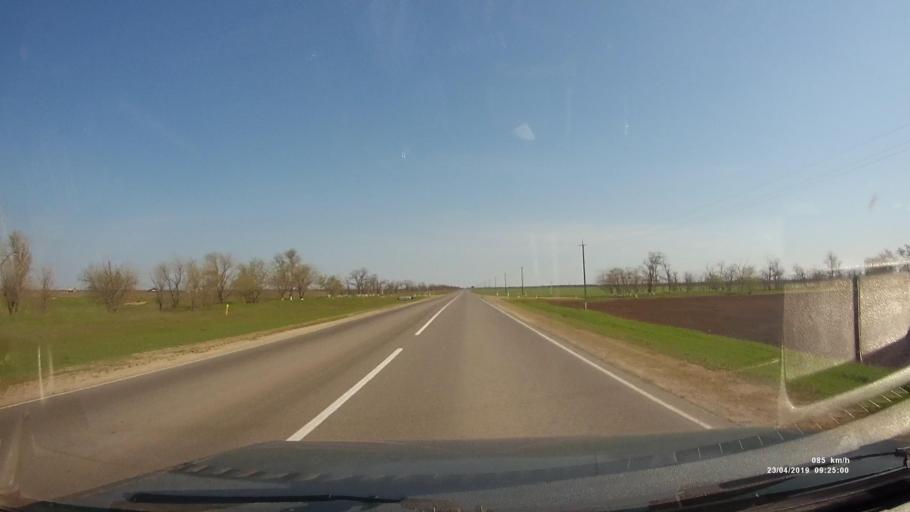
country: RU
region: Rostov
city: Proletarsk
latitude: 46.7100
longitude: 41.7593
